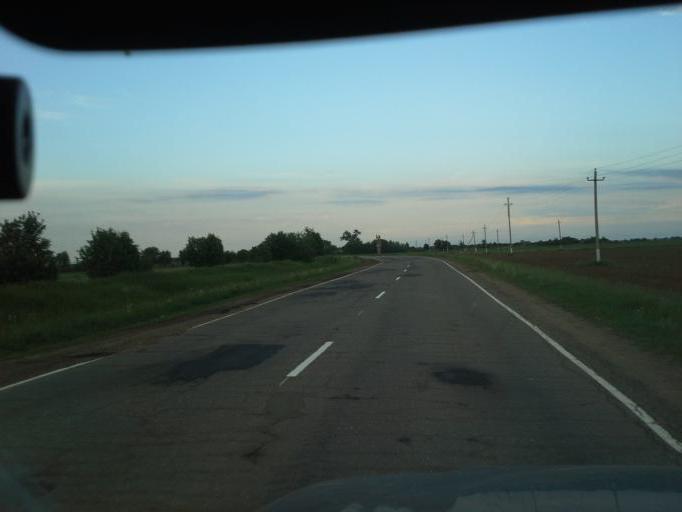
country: RU
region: Ivanovo
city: Gavrilov Posad
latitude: 56.5512
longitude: 40.1590
